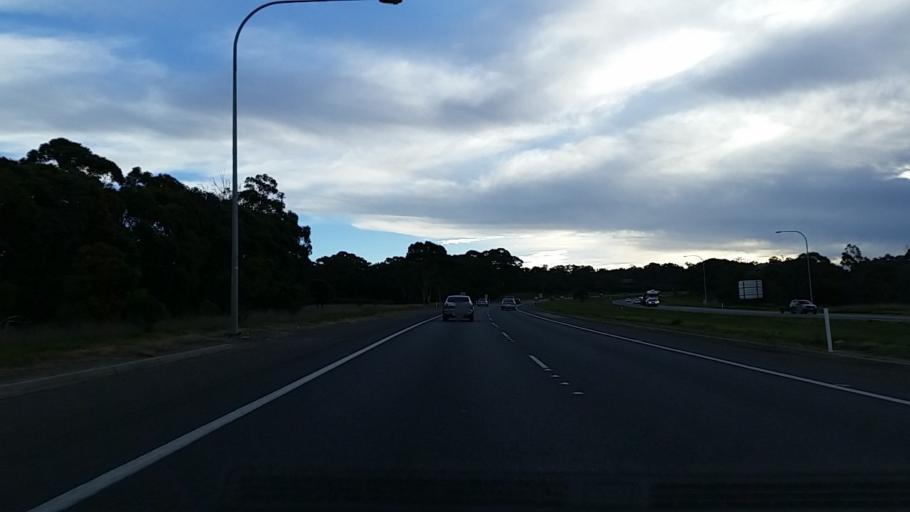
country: AU
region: South Australia
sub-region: Mount Barker
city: Little Hampton
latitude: -35.0595
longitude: 138.8450
